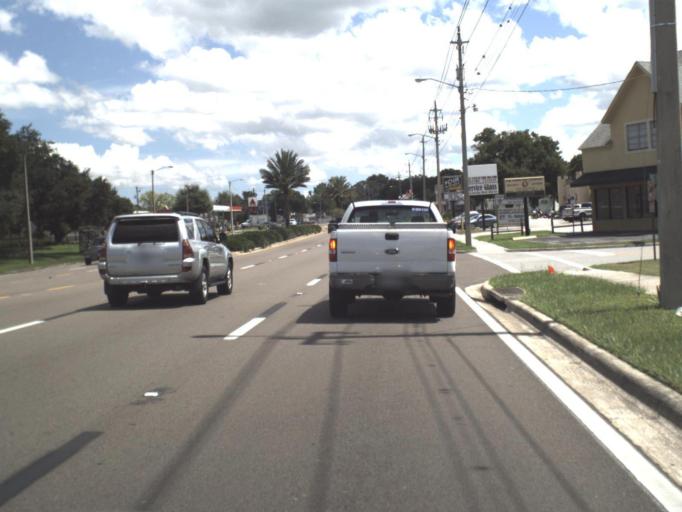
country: US
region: Florida
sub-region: Polk County
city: Inwood
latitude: 28.0455
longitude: -81.7462
